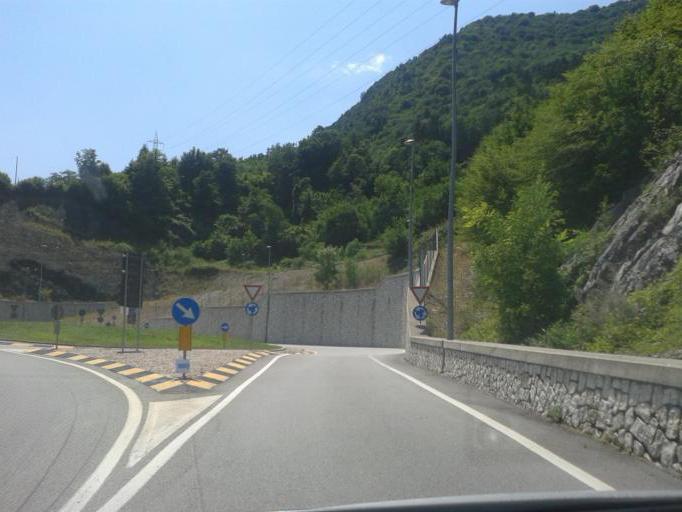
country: IT
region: Lombardy
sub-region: Provincia di Brescia
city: Ponte Caffaro
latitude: 45.8001
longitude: 10.5038
